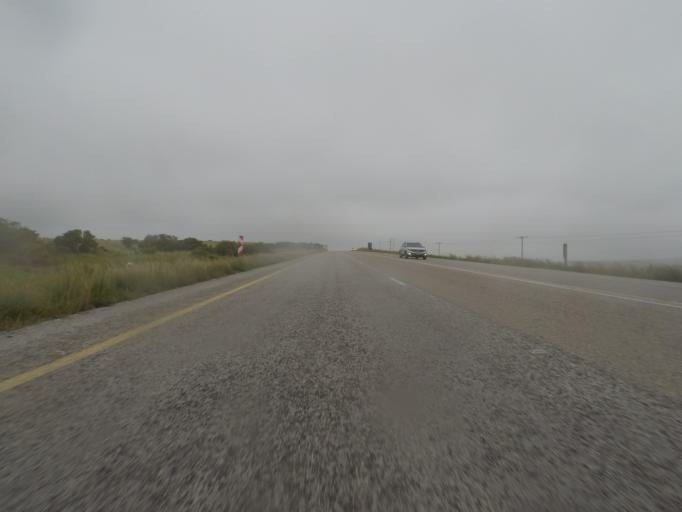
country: ZA
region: Eastern Cape
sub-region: Cacadu District Municipality
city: Grahamstown
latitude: -33.6248
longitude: 26.2990
